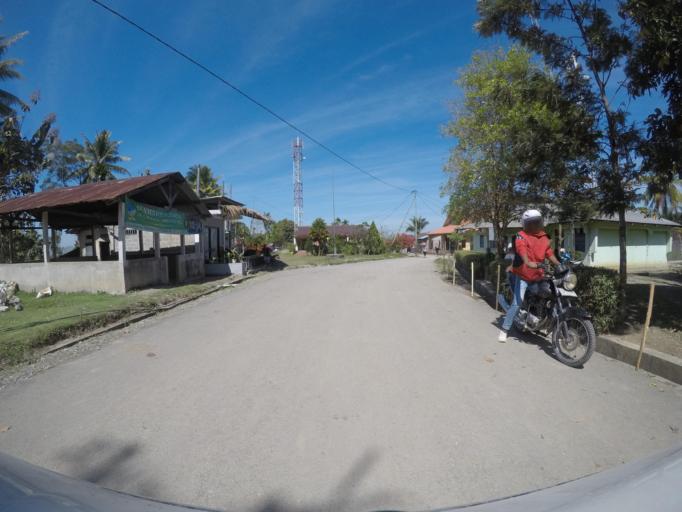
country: TL
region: Ermera
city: Gleno
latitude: -8.8119
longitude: 125.3184
